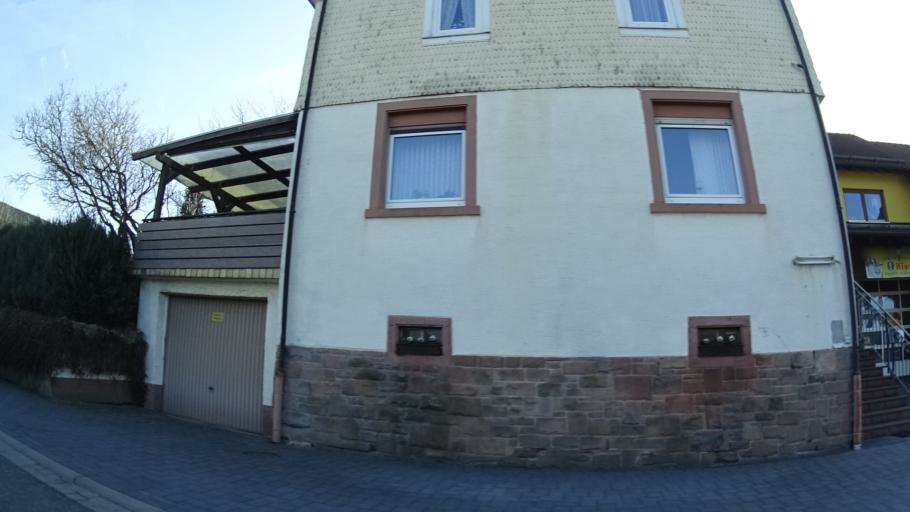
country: DE
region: Hesse
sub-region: Regierungsbezirk Darmstadt
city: Wald-Michelbach
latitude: 49.6127
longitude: 8.8565
